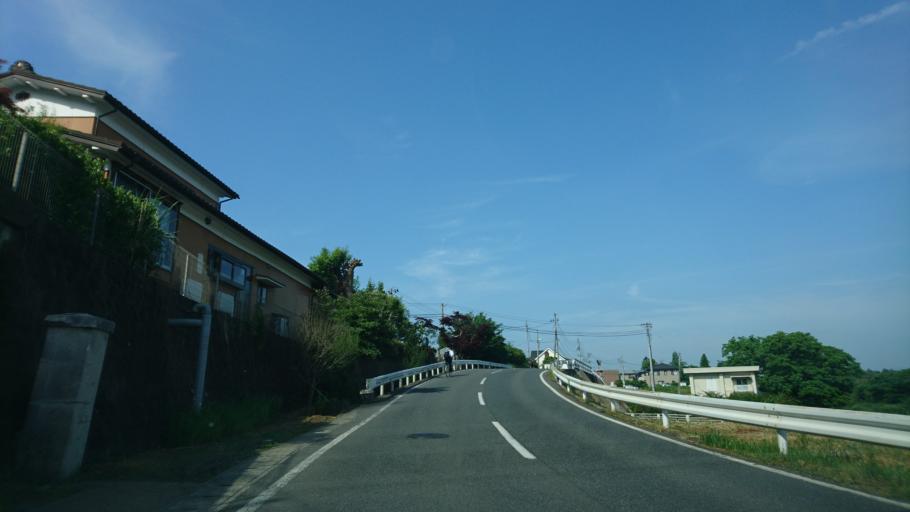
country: JP
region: Iwate
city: Ichinoseki
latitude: 38.9247
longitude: 141.1259
